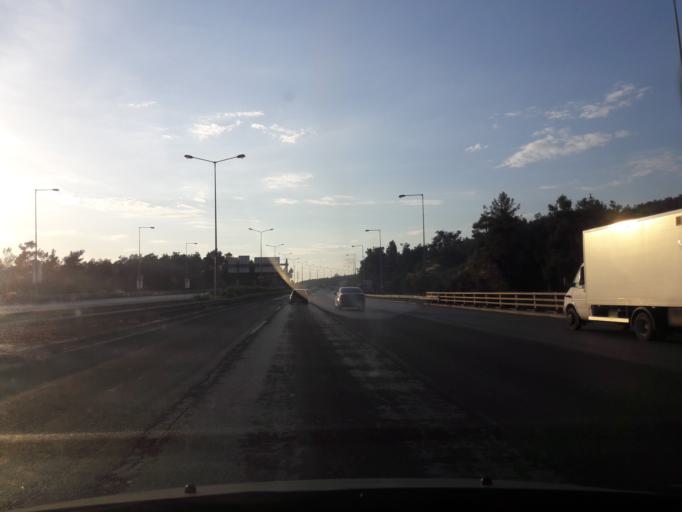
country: GR
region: Central Macedonia
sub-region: Nomos Thessalonikis
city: Triandria
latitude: 40.6288
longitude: 22.9766
